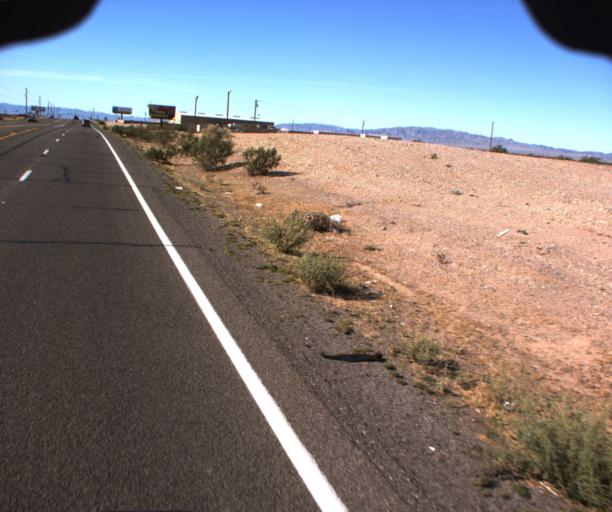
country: US
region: Arizona
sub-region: Mohave County
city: Mohave Valley
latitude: 34.9885
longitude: -114.5981
